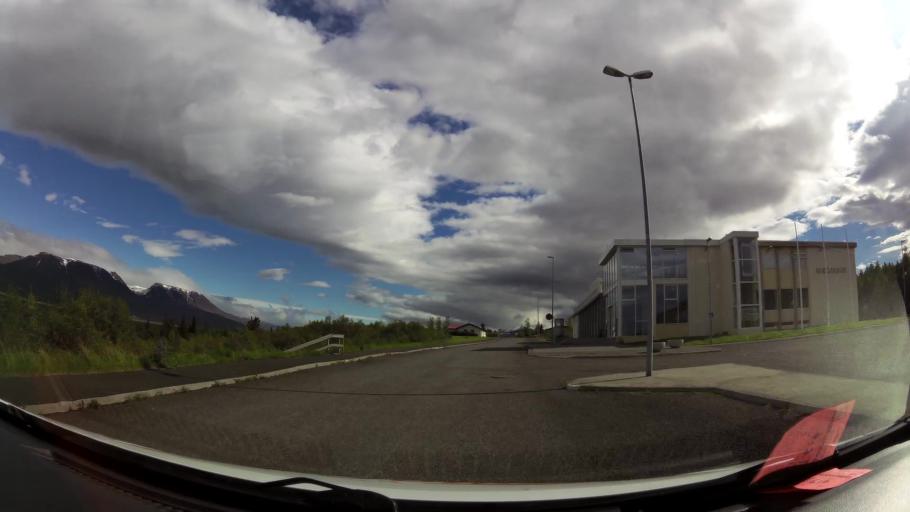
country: IS
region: Northwest
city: Saudarkrokur
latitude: 65.5523
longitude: -19.4493
